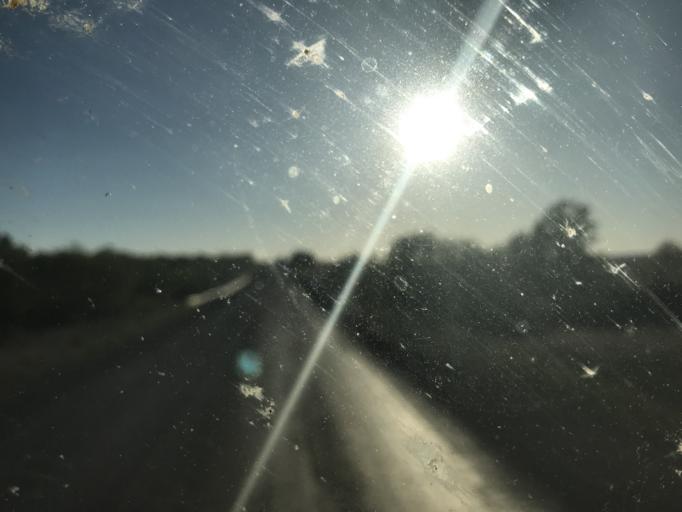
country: KZ
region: Aqtoebe
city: Aqtobe
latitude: 50.2902
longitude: 57.6736
